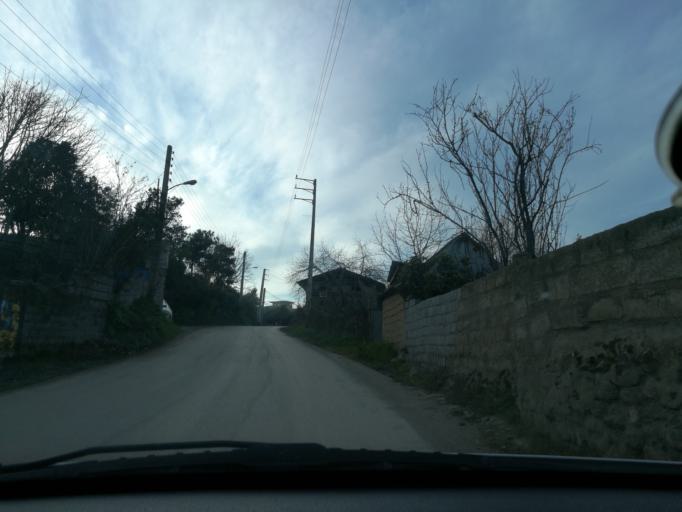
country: IR
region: Mazandaran
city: Chalus
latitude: 36.6431
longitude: 51.4374
